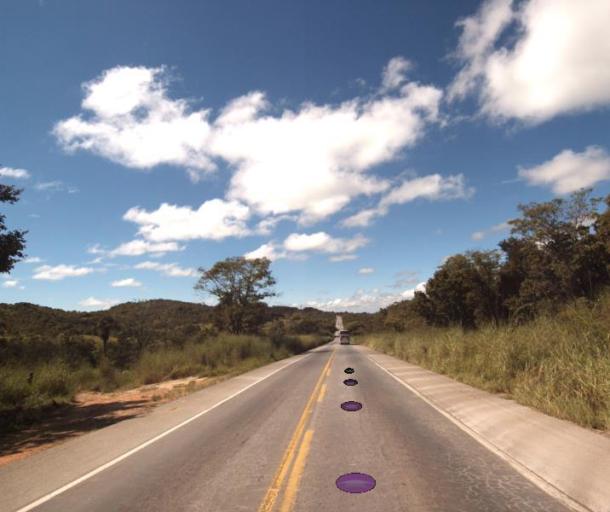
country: BR
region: Goias
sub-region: Uruana
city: Uruana
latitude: -15.5030
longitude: -49.4800
